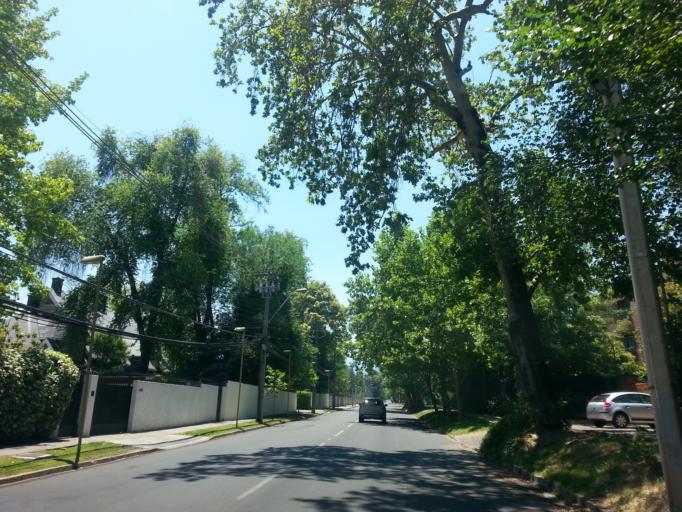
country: CL
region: Santiago Metropolitan
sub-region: Provincia de Santiago
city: Villa Presidente Frei, Nunoa, Santiago, Chile
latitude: -33.3850
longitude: -70.5283
